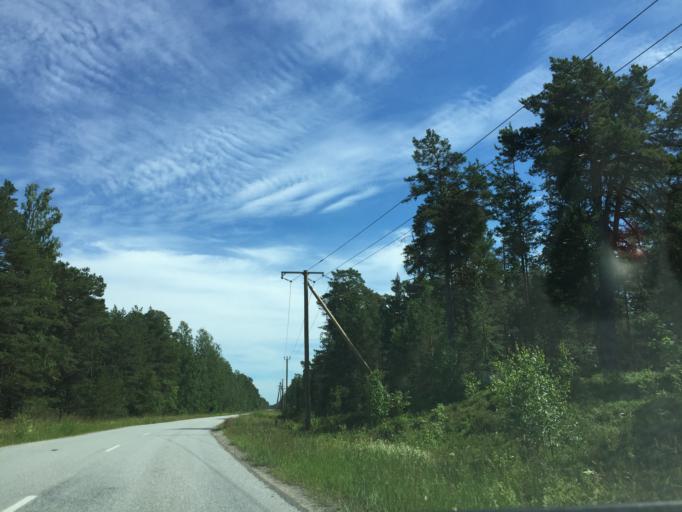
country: LV
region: Rojas
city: Roja
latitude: 57.5698
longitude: 22.6452
